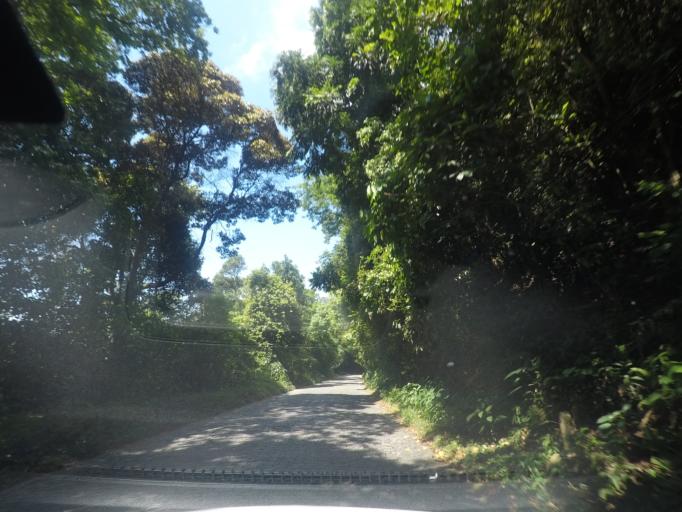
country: BR
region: Rio de Janeiro
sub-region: Petropolis
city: Petropolis
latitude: -22.5497
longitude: -43.1825
